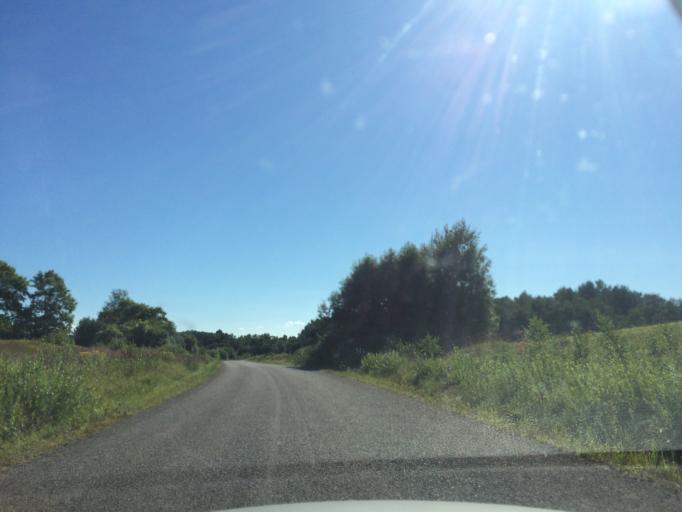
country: LV
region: Rezekne
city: Rezekne
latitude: 56.5048
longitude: 27.2992
